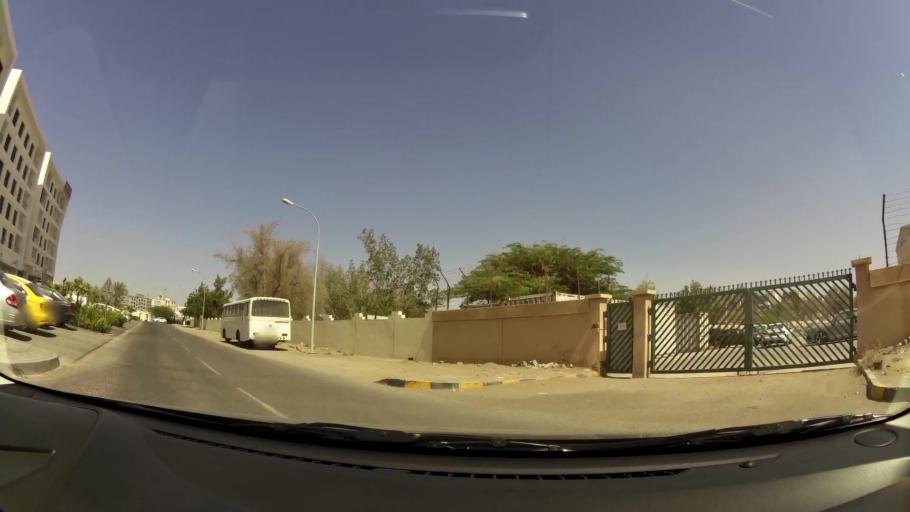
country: OM
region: Muhafazat Masqat
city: Bawshar
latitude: 23.5927
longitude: 58.3627
